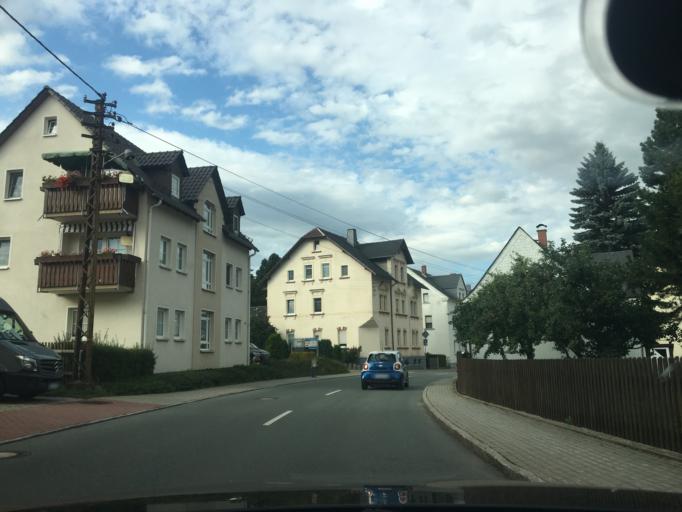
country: DE
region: Saxony
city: Oelsnitz
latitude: 50.7174
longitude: 12.6814
